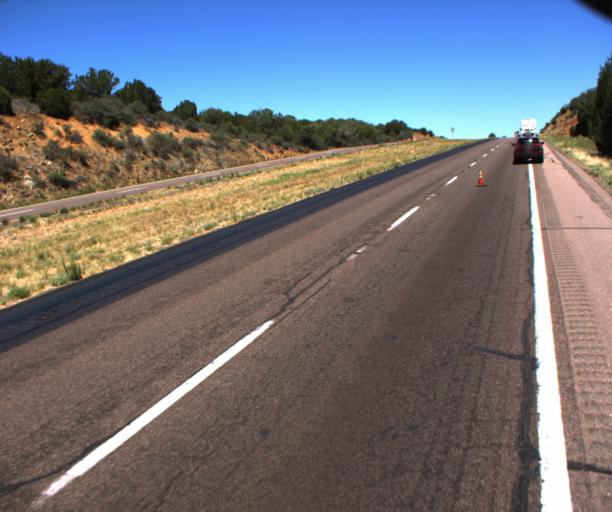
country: US
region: Arizona
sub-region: Gila County
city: Payson
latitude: 34.1685
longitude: -111.3350
